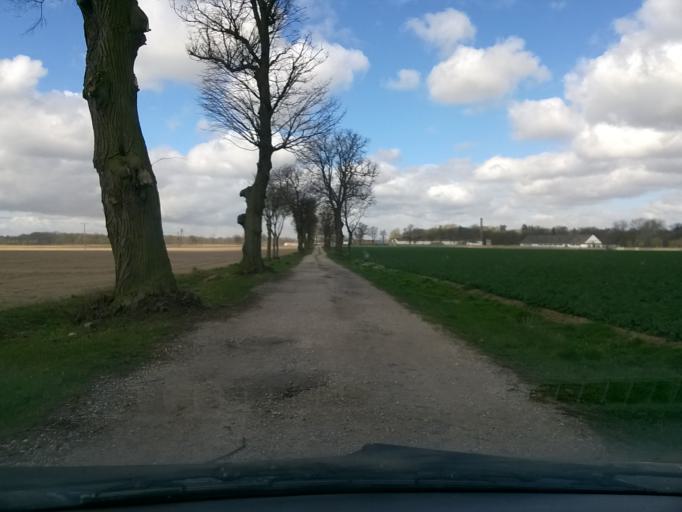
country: PL
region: Kujawsko-Pomorskie
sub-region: Powiat nakielski
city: Kcynia
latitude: 52.9844
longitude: 17.4325
